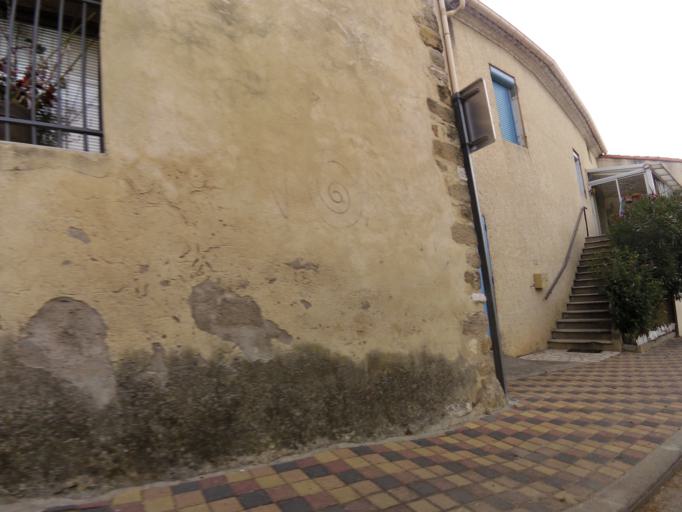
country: FR
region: Languedoc-Roussillon
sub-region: Departement du Gard
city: Saint-Mamert-du-Gard
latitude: 43.9201
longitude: 4.1979
